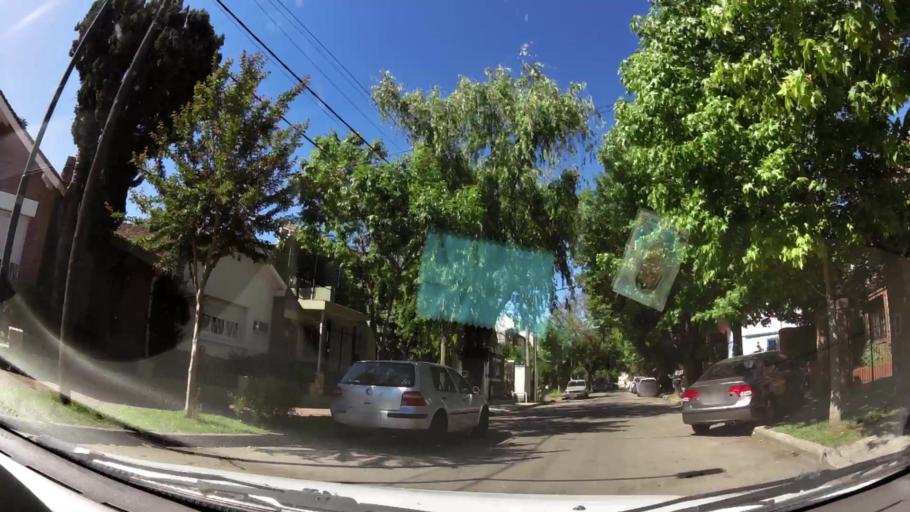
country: AR
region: Buenos Aires
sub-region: Partido de San Isidro
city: San Isidro
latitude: -34.4544
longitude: -58.5278
